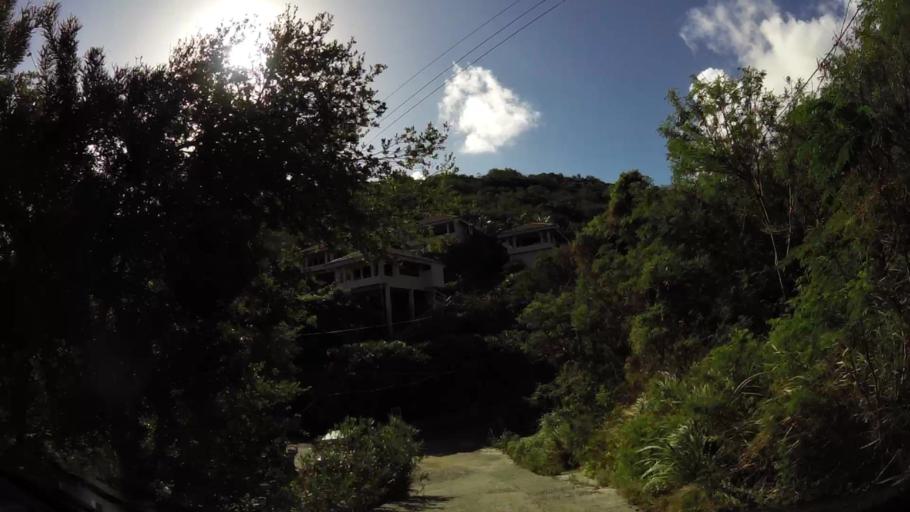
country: VG
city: Tortola
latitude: 18.4971
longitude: -64.3838
